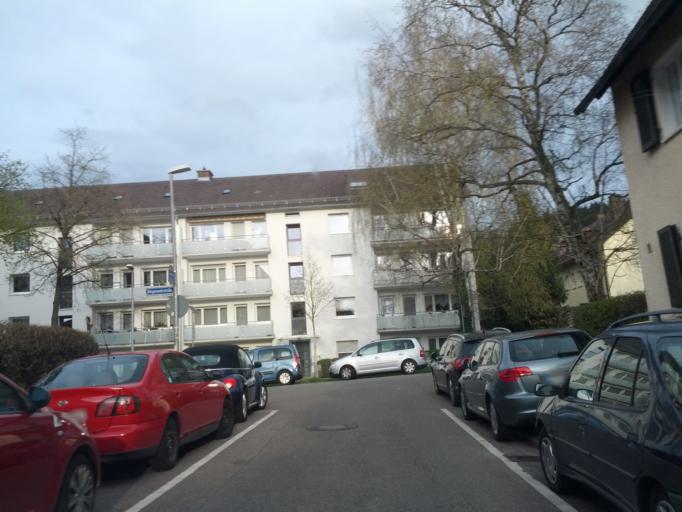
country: DE
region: Baden-Wuerttemberg
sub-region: Freiburg Region
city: Freiburg
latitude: 47.9857
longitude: 7.8620
